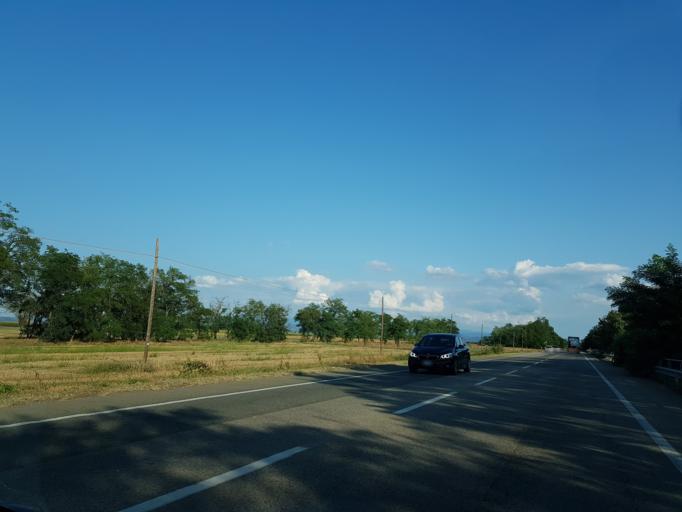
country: IT
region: Piedmont
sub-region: Provincia di Alessandria
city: Litta Parodi-Cascinagrossa
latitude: 44.8505
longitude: 8.7197
